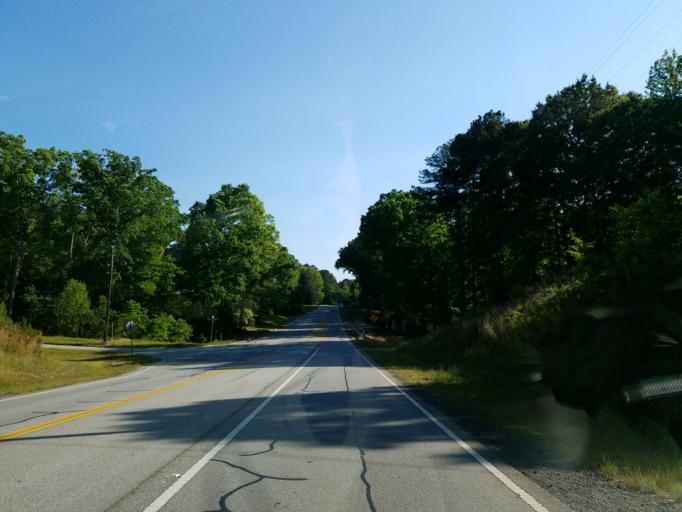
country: US
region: Georgia
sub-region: Paulding County
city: Dallas
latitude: 33.9007
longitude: -84.8767
